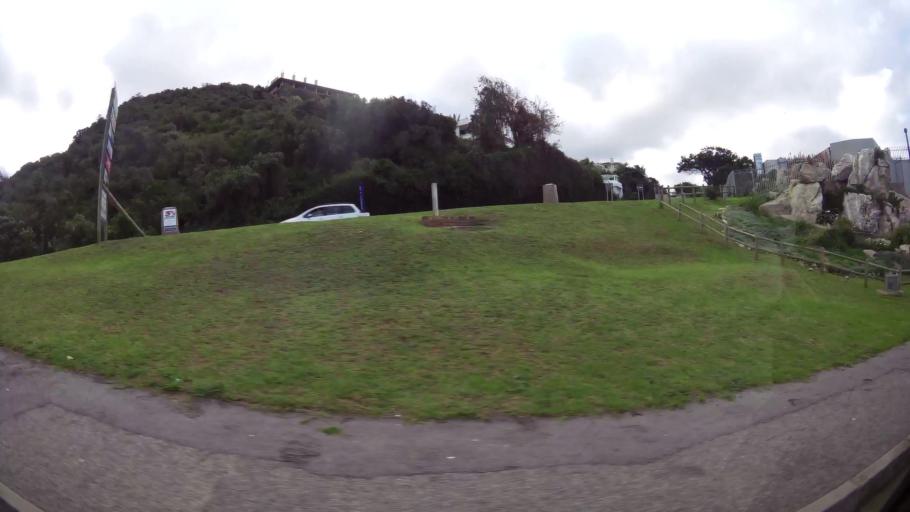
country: ZA
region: Western Cape
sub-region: Eden District Municipality
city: Plettenberg Bay
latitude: -34.0605
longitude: 23.3762
